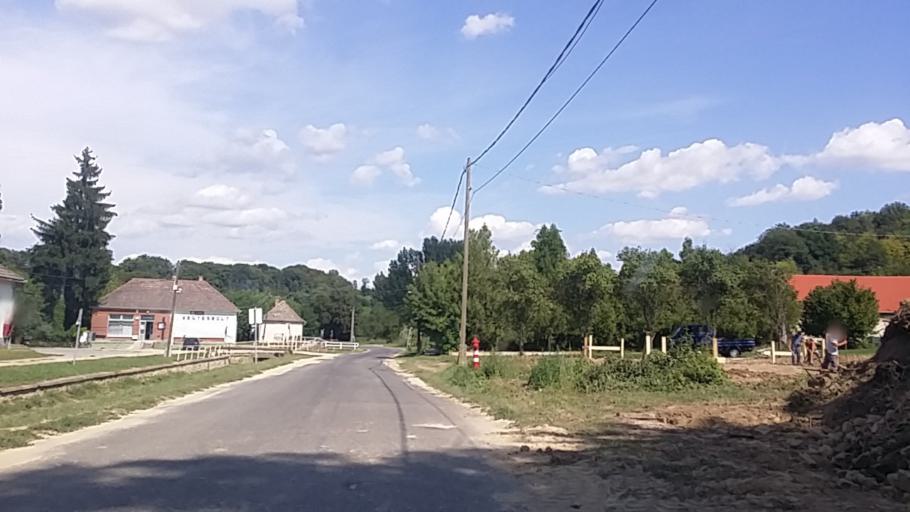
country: HU
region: Tolna
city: Gyonk
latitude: 46.5372
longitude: 18.4701
